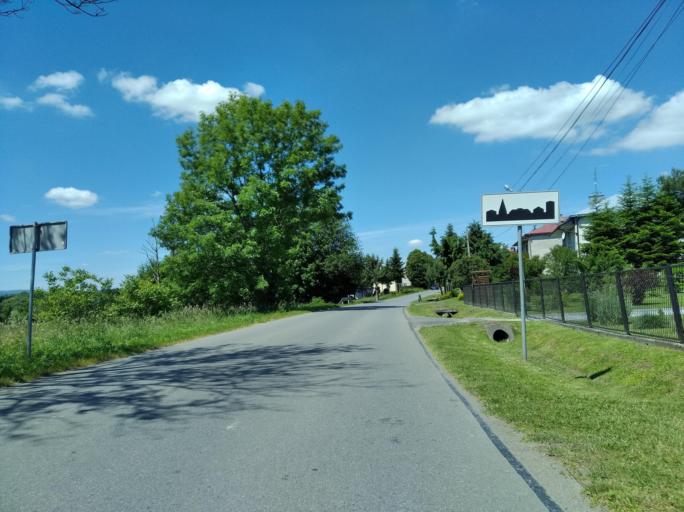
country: PL
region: Subcarpathian Voivodeship
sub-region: Powiat jasielski
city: Nowy Zmigrod
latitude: 49.6200
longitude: 21.5499
